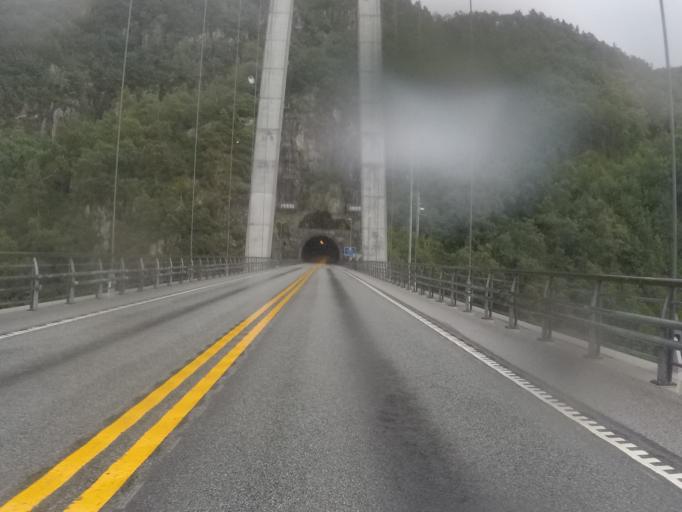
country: NO
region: Vest-Agder
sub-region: Kvinesdal
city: Liknes
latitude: 58.2607
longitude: 6.8466
